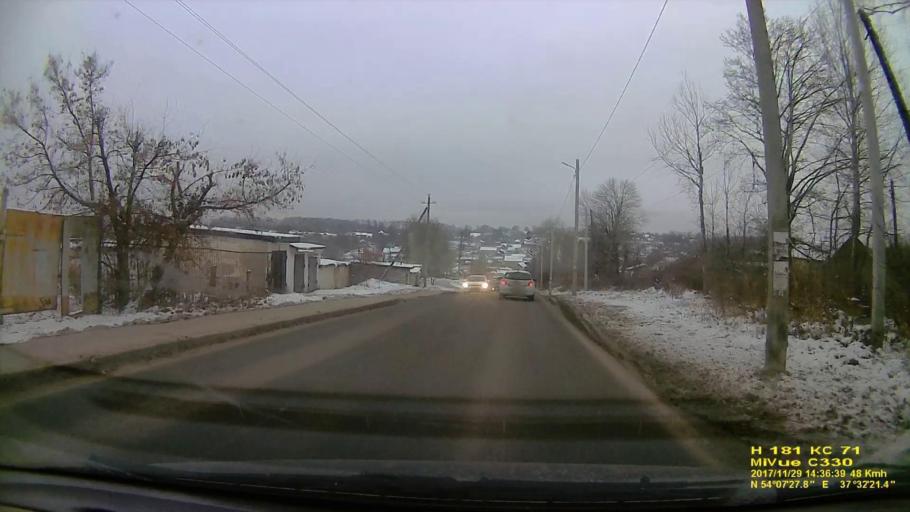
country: RU
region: Tula
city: Kosaya Gora
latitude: 54.1242
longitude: 37.5393
